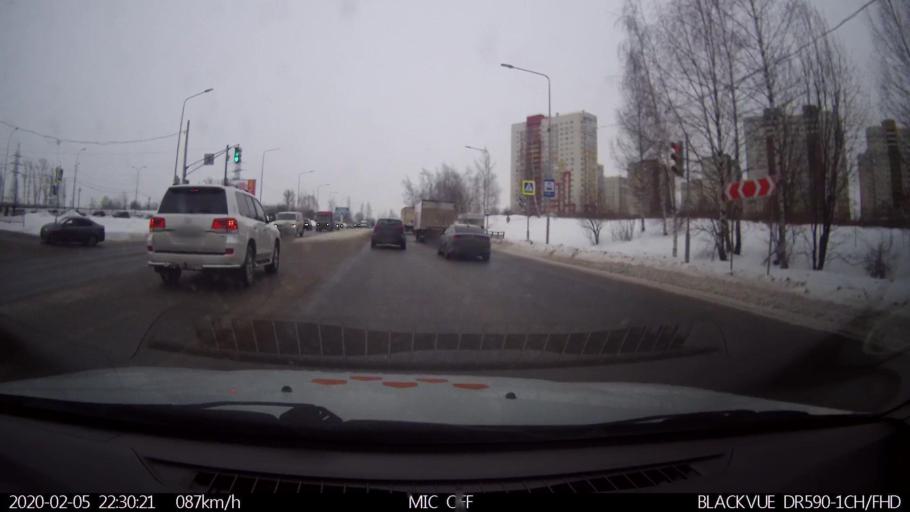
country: RU
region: Nizjnij Novgorod
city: Imeni Stepana Razina
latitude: 54.7435
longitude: 44.1594
